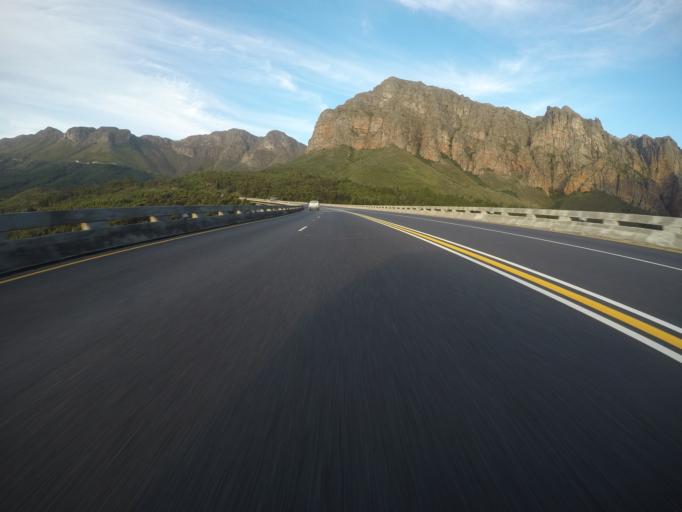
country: ZA
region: Western Cape
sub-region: Cape Winelands District Municipality
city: Paarl
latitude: -33.7454
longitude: 19.0607
